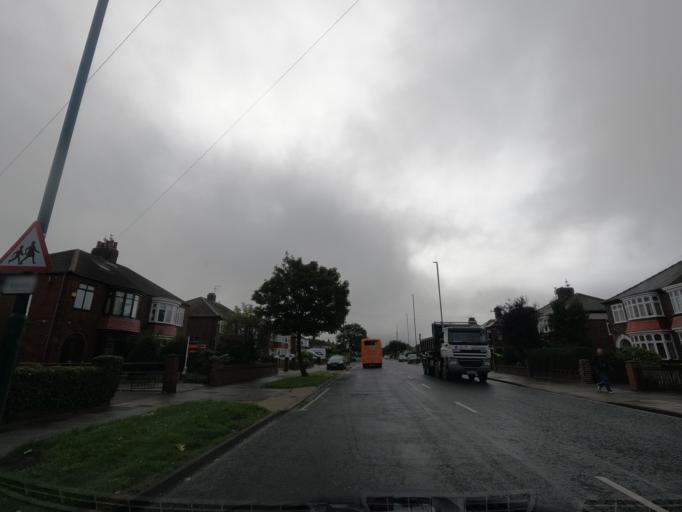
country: GB
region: England
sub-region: Redcar and Cleveland
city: Redcar
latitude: 54.6123
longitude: -1.0841
